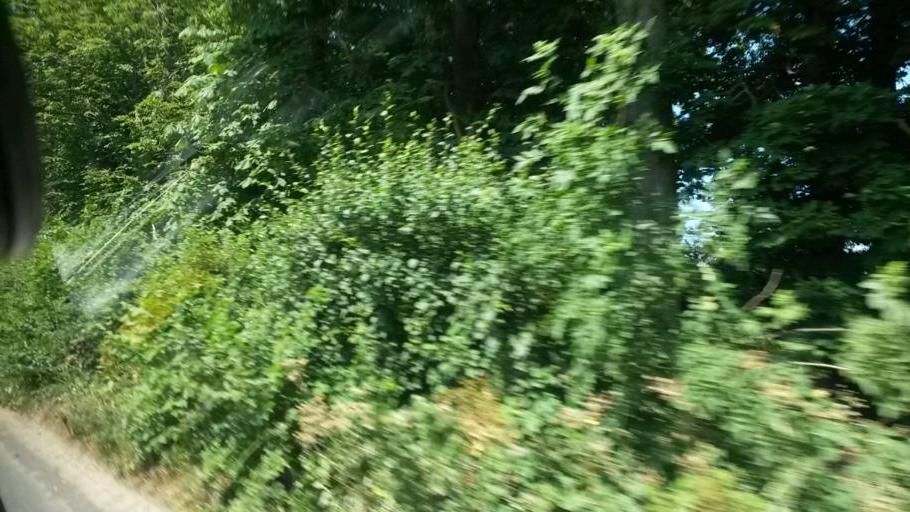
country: IE
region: Leinster
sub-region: Fingal County
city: Swords
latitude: 53.5150
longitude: -6.2413
